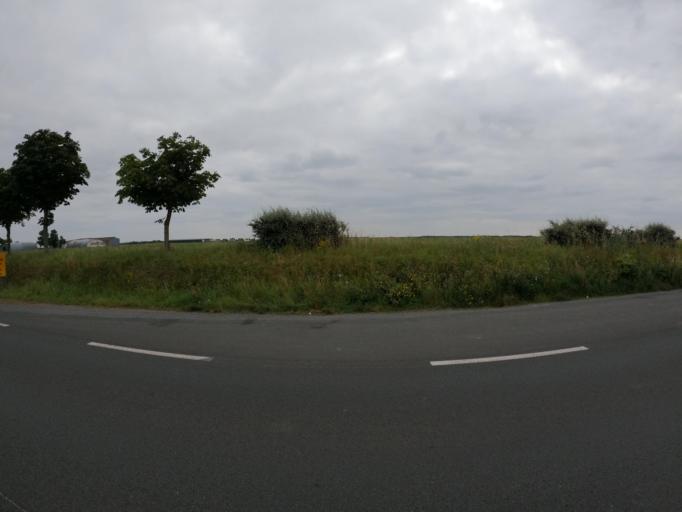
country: FR
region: Pays de la Loire
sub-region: Departement de la Vendee
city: Fontenay-le-Comte
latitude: 46.4431
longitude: -0.7936
